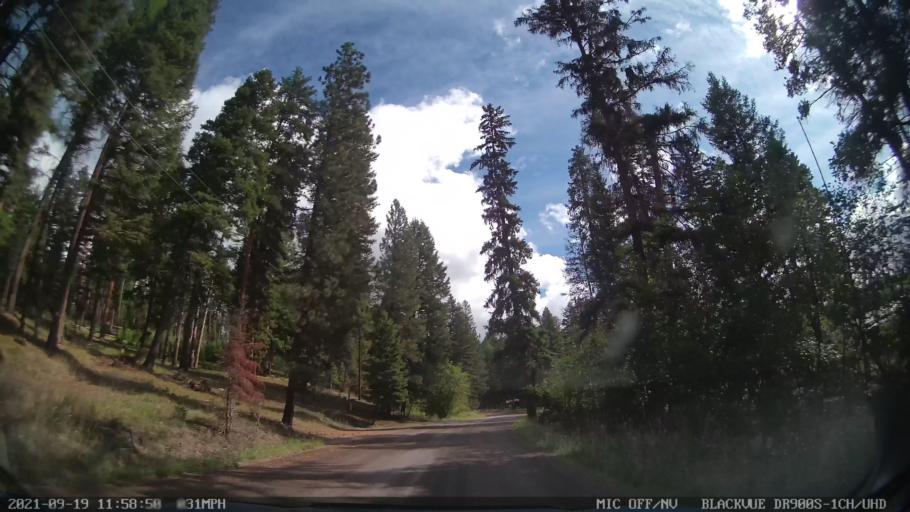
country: US
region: Montana
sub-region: Missoula County
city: Seeley Lake
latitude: 47.1829
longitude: -113.4824
